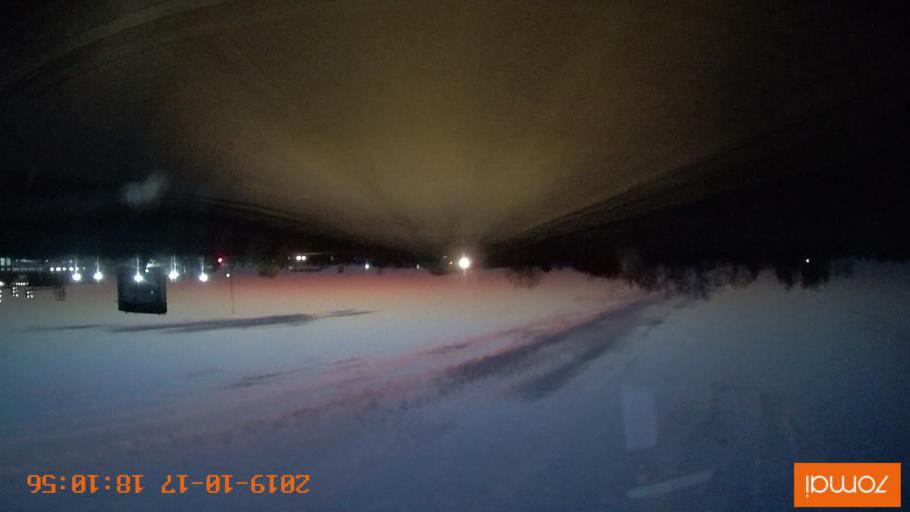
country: RU
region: Tula
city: Kurkino
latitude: 53.4183
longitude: 38.6361
